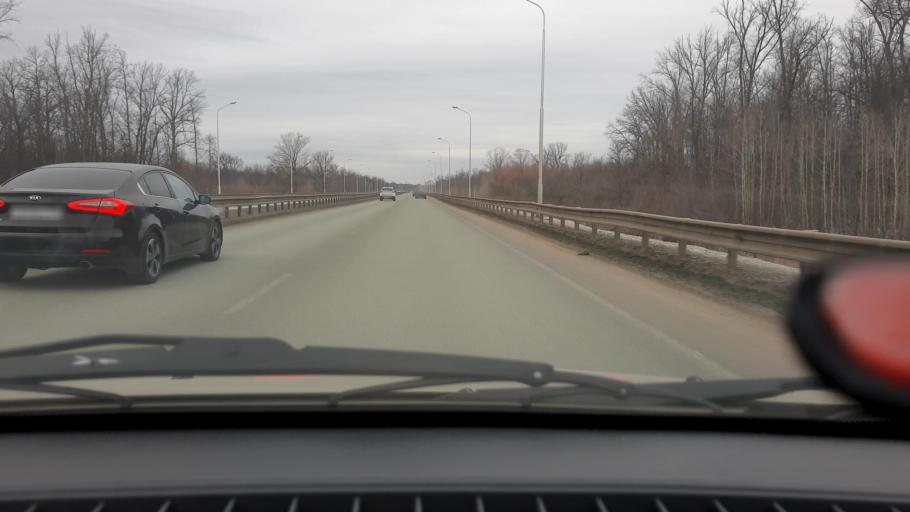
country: RU
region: Bashkortostan
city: Ufa
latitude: 54.6695
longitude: 56.0467
